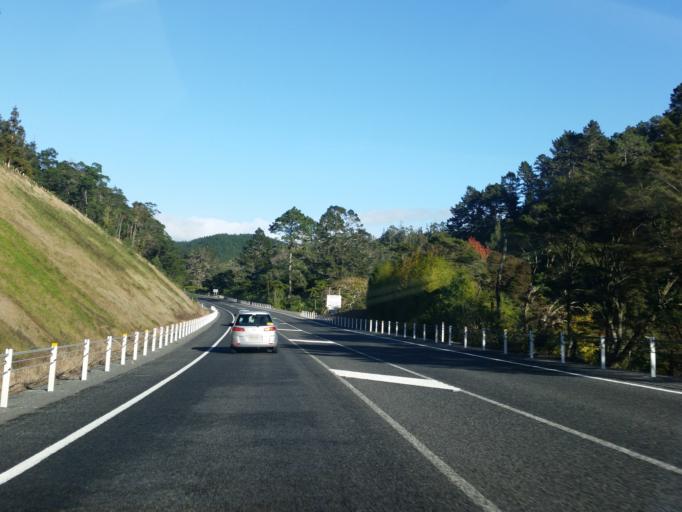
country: NZ
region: Bay of Plenty
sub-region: Western Bay of Plenty District
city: Waihi Beach
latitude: -37.4585
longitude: 175.9233
